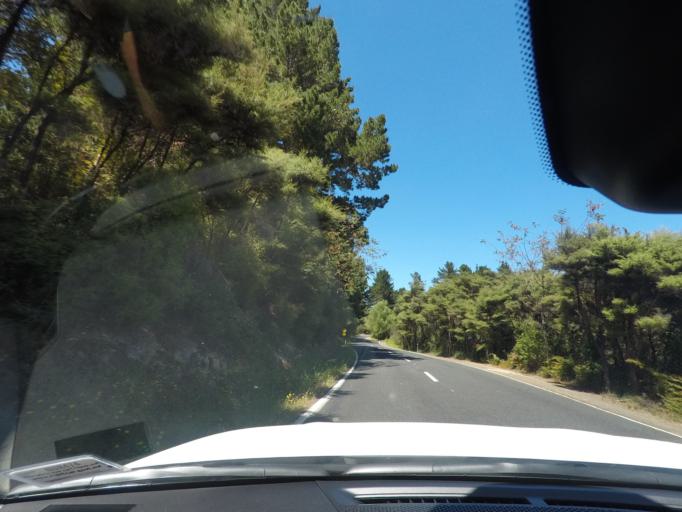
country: NZ
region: Auckland
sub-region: Auckland
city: Parakai
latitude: -36.5744
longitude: 174.3562
